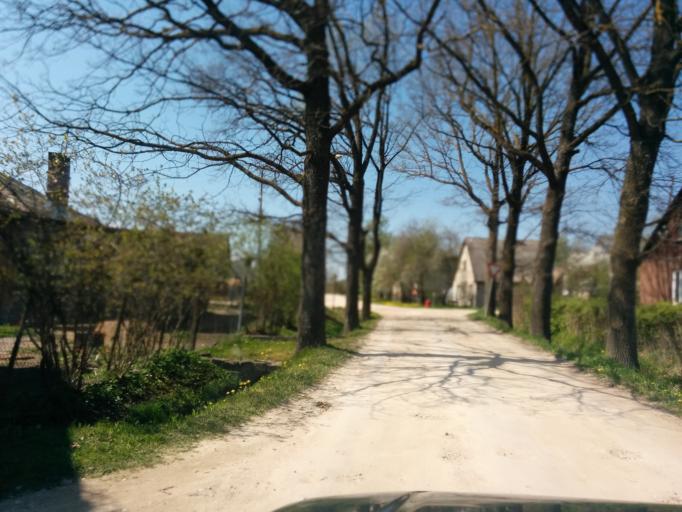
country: LV
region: Jelgava
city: Jelgava
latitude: 56.6238
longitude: 23.7310
